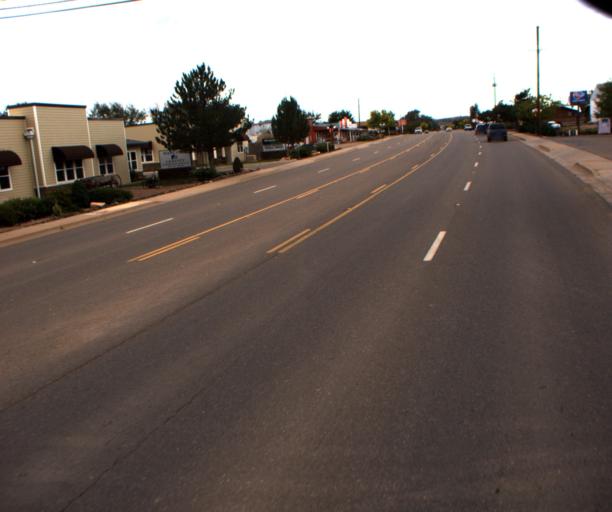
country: US
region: Arizona
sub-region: Navajo County
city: Taylor
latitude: 34.4678
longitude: -110.0913
